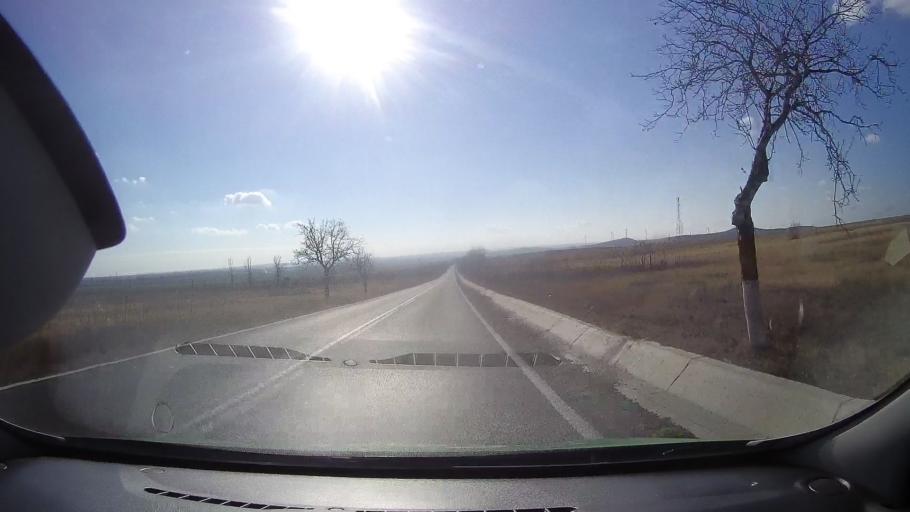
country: RO
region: Tulcea
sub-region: Comuna Ceamurlia de Jos
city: Ceamurlia de Jos
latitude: 44.8132
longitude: 28.6915
